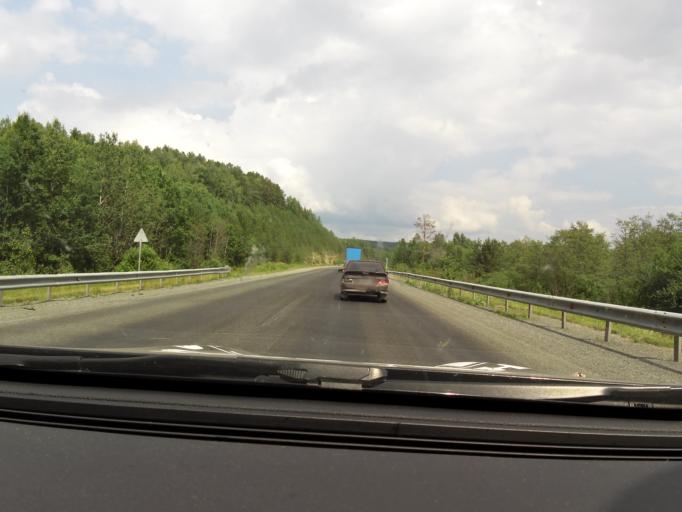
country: RU
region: Sverdlovsk
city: Ufimskiy
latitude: 56.7732
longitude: 58.2165
